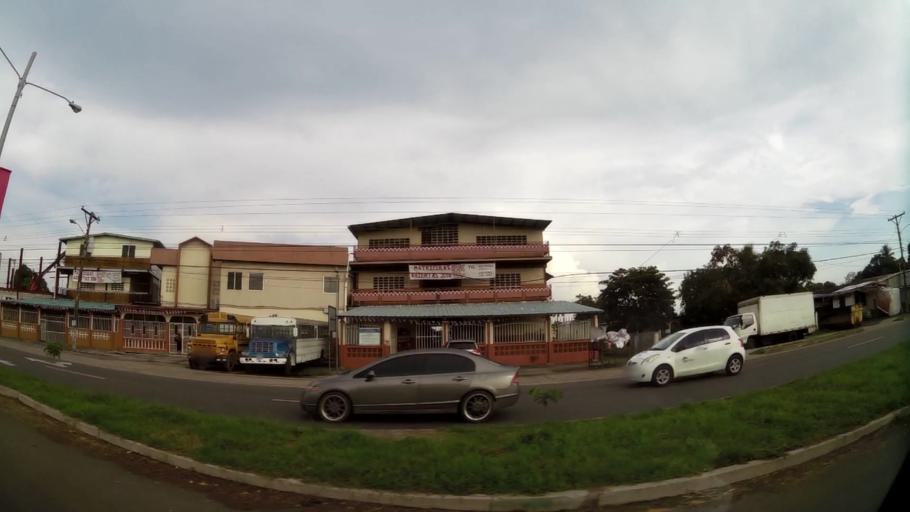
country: PA
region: Panama
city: Tocumen
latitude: 9.0862
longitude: -79.3665
